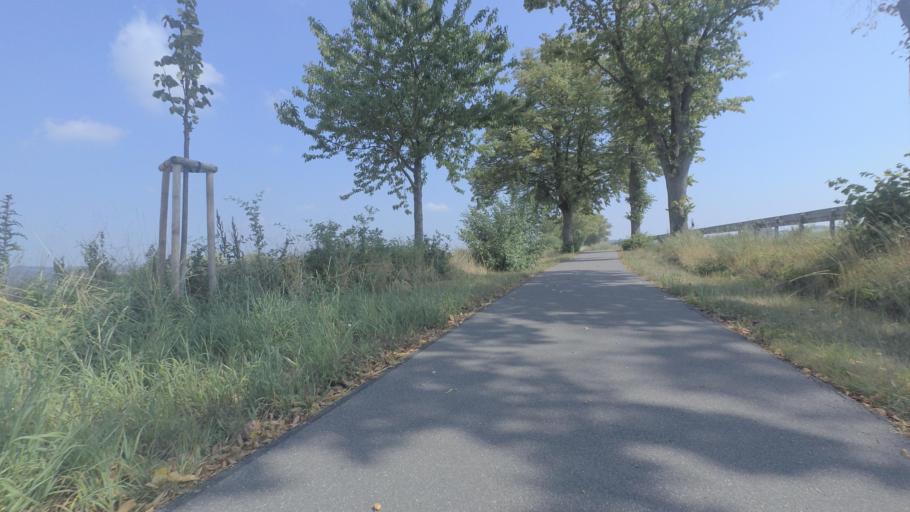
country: DE
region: Mecklenburg-Vorpommern
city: Gielow
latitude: 53.7288
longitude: 12.7318
